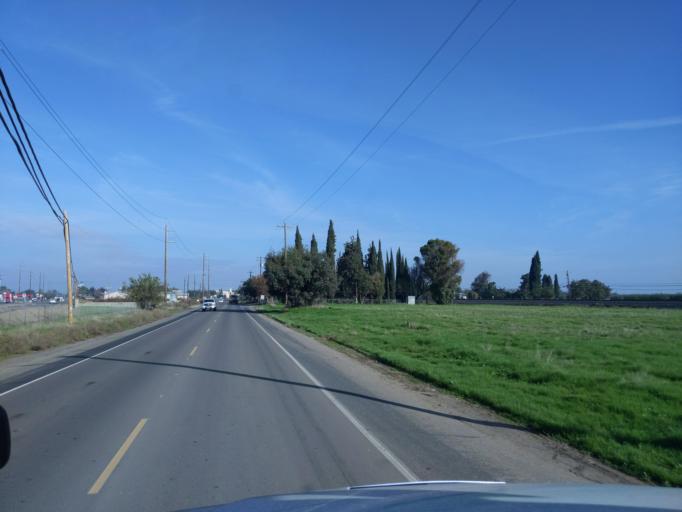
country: US
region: California
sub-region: San Joaquin County
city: French Camp
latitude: 37.8765
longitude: -121.2758
